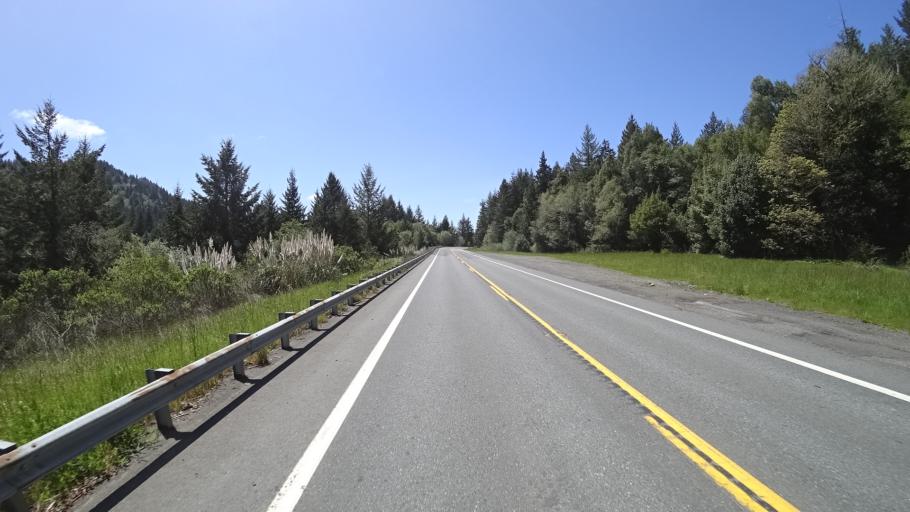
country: US
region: California
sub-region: Humboldt County
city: Blue Lake
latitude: 40.8921
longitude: -123.9366
